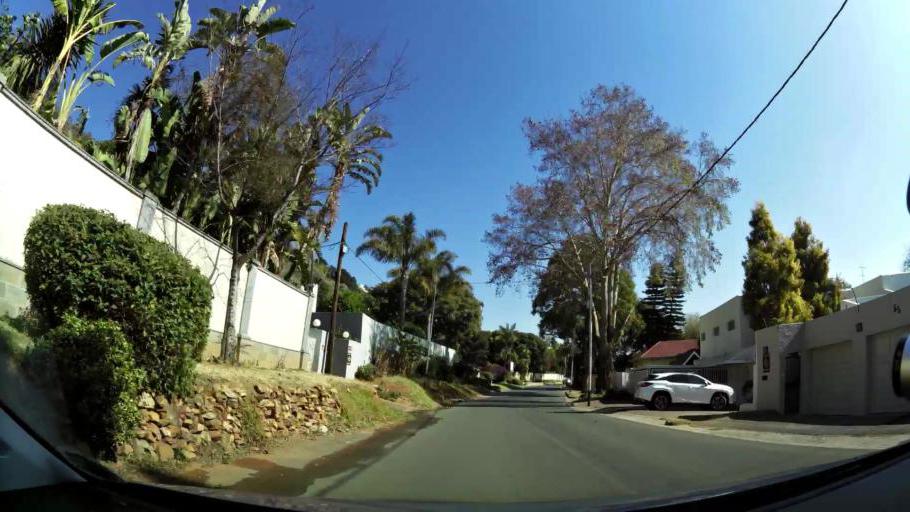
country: ZA
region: Gauteng
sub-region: City of Johannesburg Metropolitan Municipality
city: Johannesburg
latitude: -26.1657
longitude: 28.1001
